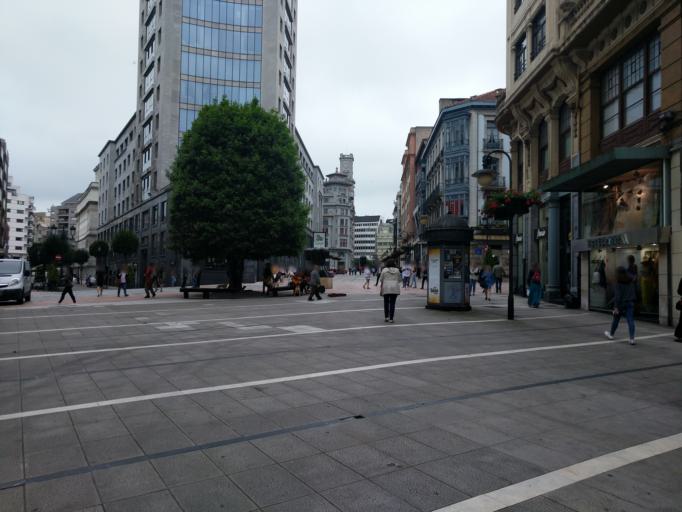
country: ES
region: Asturias
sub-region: Province of Asturias
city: Oviedo
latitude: 43.3639
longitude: -5.8493
